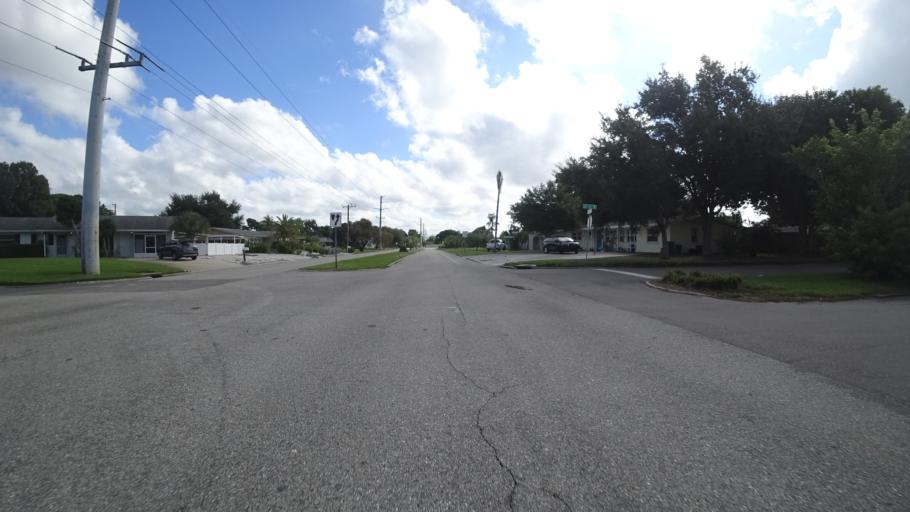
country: US
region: Florida
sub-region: Manatee County
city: West Bradenton
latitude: 27.4996
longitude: -82.6225
